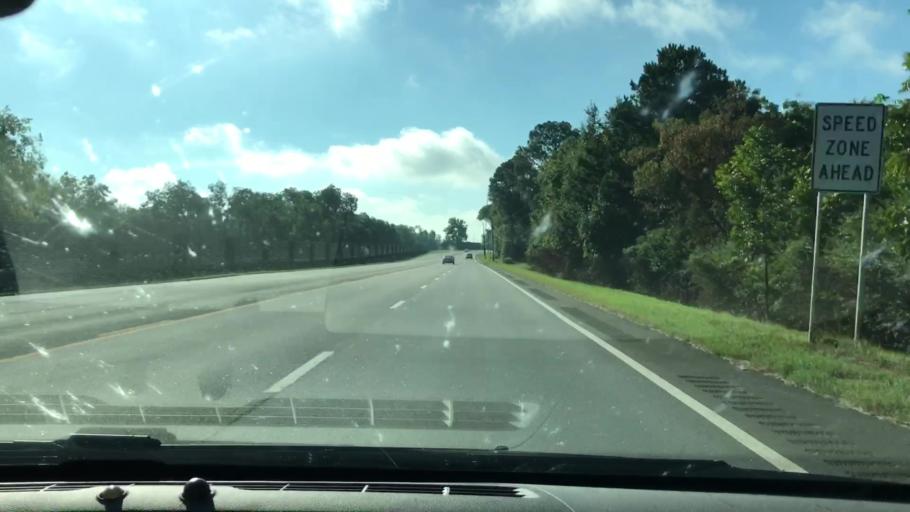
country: US
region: Georgia
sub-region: Terrell County
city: Dawson
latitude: 31.7235
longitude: -84.3536
